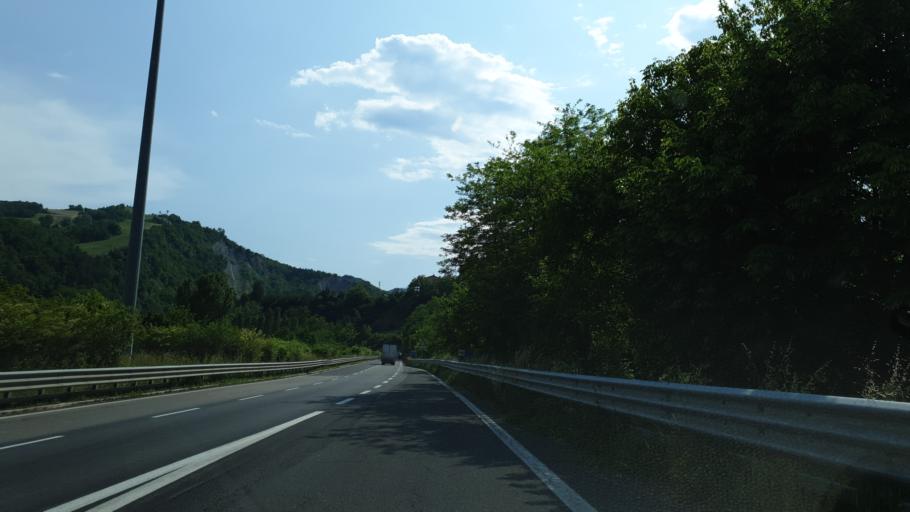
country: IT
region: Emilia-Romagna
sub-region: Forli-Cesena
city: Sarsina
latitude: 43.9209
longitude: 12.1490
